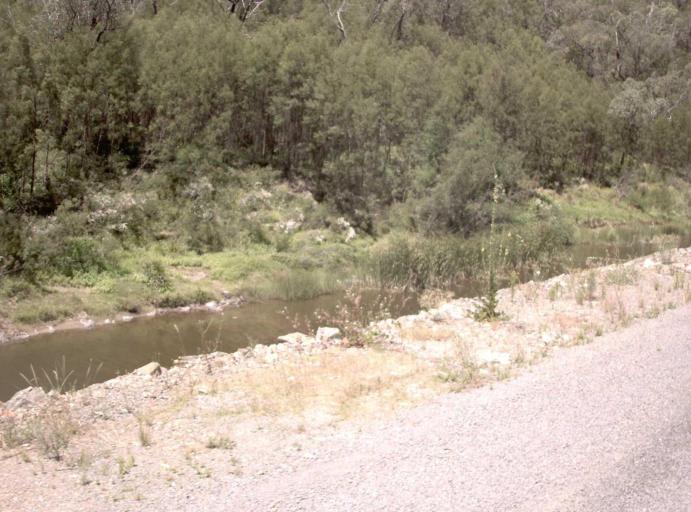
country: AU
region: Victoria
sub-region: East Gippsland
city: Bairnsdale
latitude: -37.4415
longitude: 147.8319
